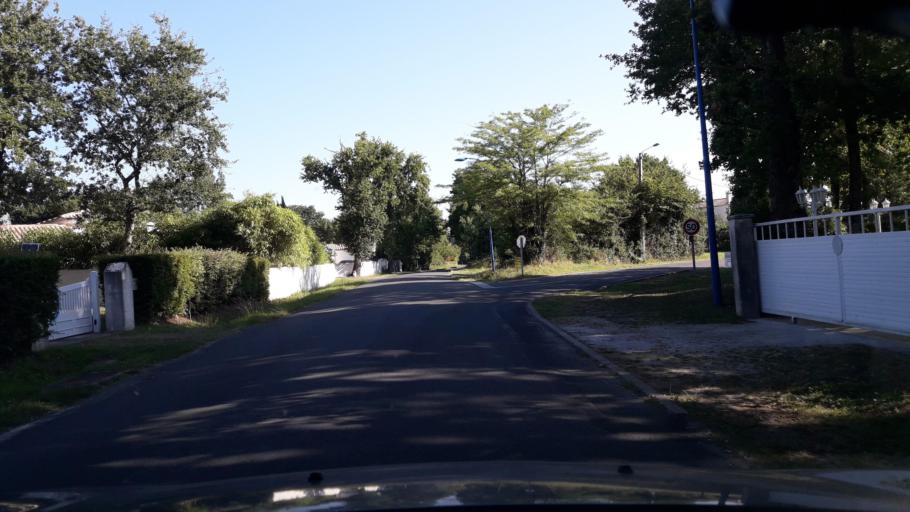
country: FR
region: Poitou-Charentes
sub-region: Departement de la Charente-Maritime
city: Etaules
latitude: 45.7196
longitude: -1.1055
